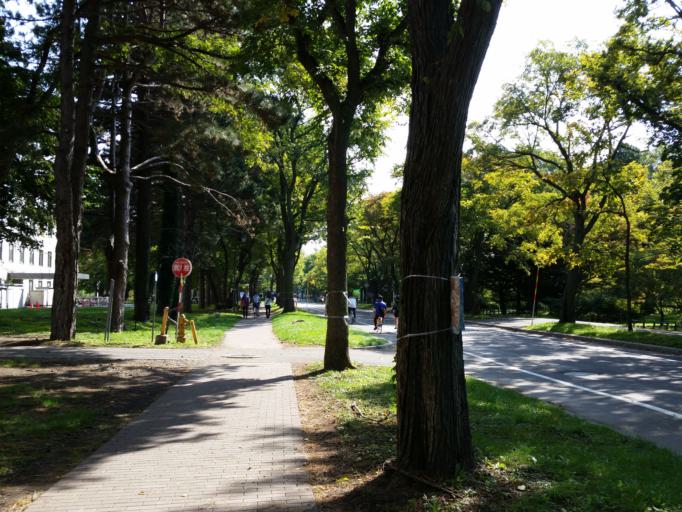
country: JP
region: Hokkaido
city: Sapporo
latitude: 43.0763
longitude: 141.3417
